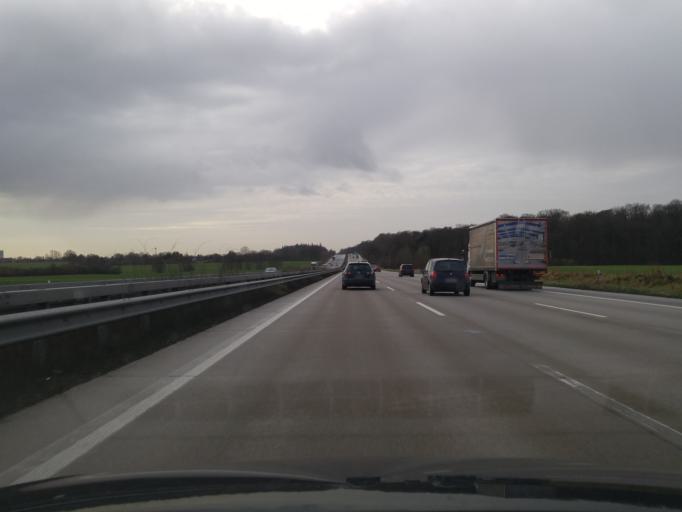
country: DE
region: Schleswig-Holstein
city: Politz
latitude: 53.7581
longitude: 10.3767
